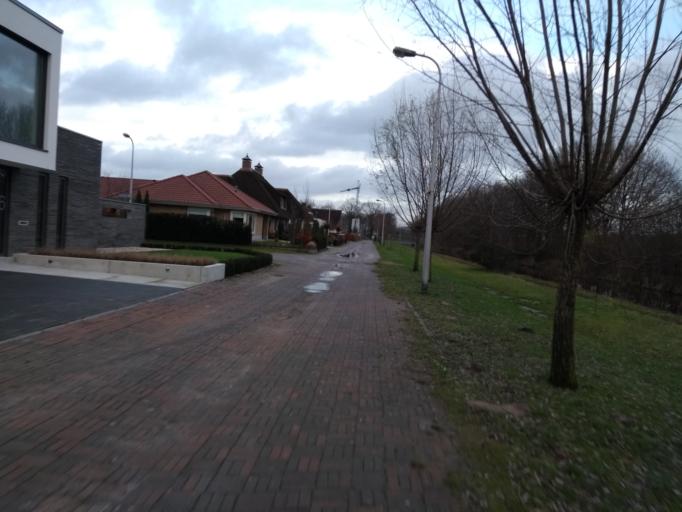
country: NL
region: Overijssel
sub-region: Gemeente Almelo
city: Almelo
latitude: 52.3713
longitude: 6.7006
